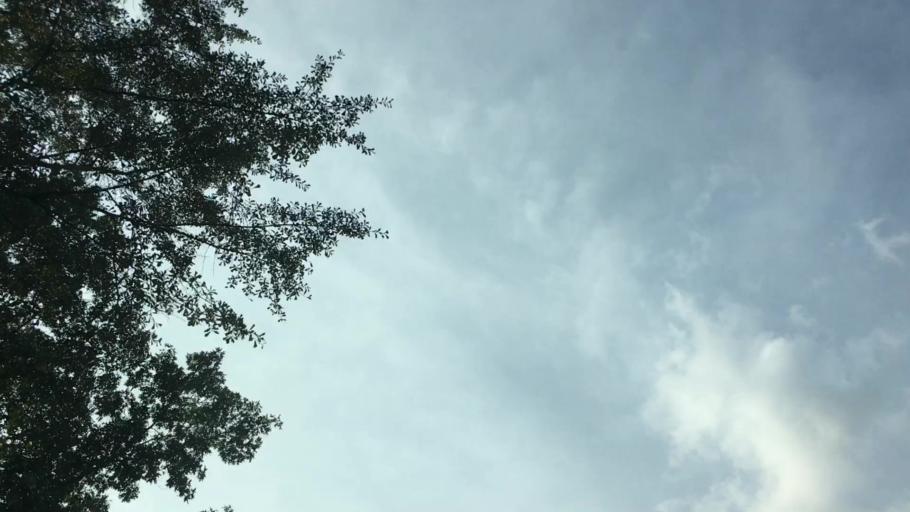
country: US
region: Alabama
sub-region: Bibb County
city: Woodstock
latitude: 33.2223
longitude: -87.1229
